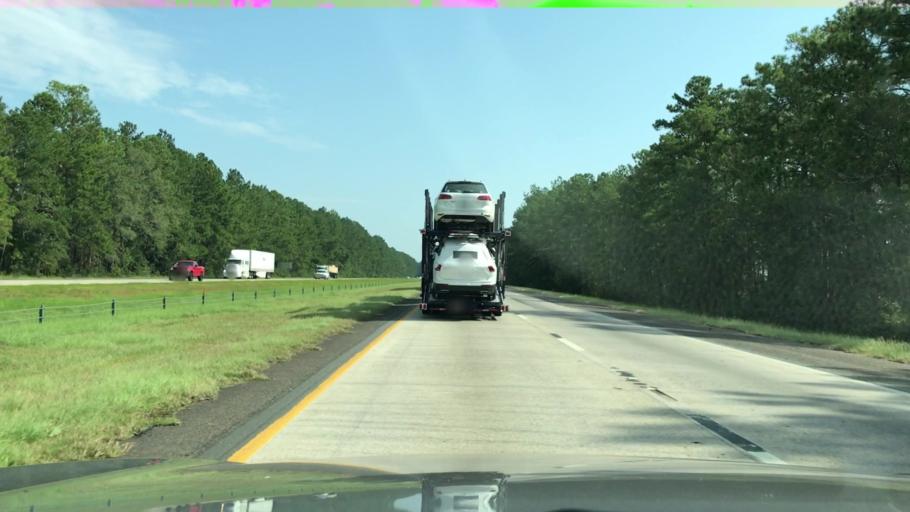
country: US
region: South Carolina
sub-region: Colleton County
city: Walterboro
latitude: 32.8137
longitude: -80.7623
